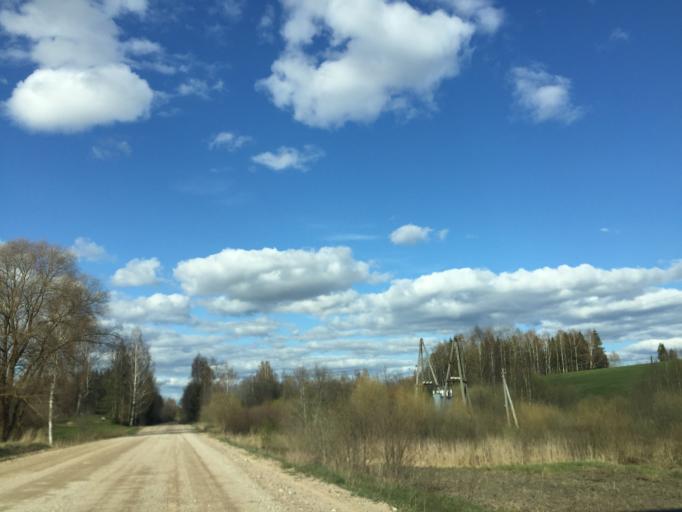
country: LV
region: Rezekne
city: Rezekne
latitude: 56.6334
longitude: 27.3090
